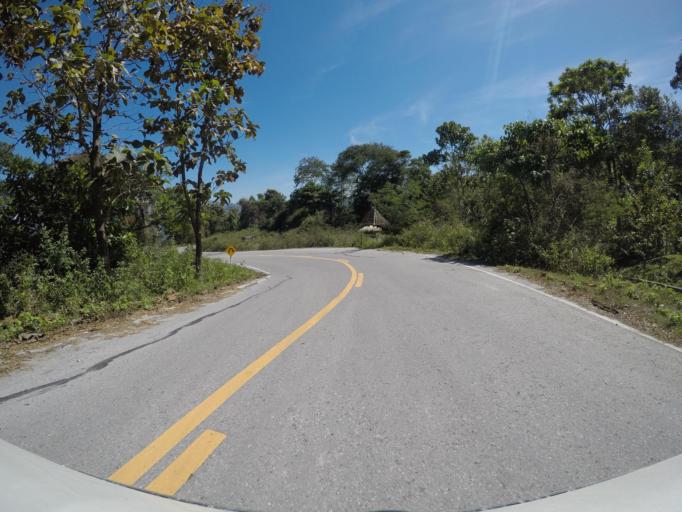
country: TL
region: Manufahi
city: Same
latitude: -8.9093
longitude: 125.9746
